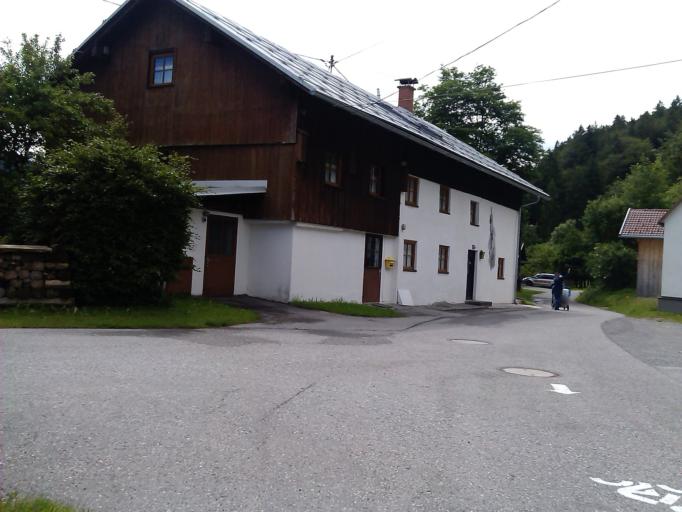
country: AT
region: Tyrol
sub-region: Politischer Bezirk Reutte
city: Pflach
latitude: 47.5117
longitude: 10.7065
